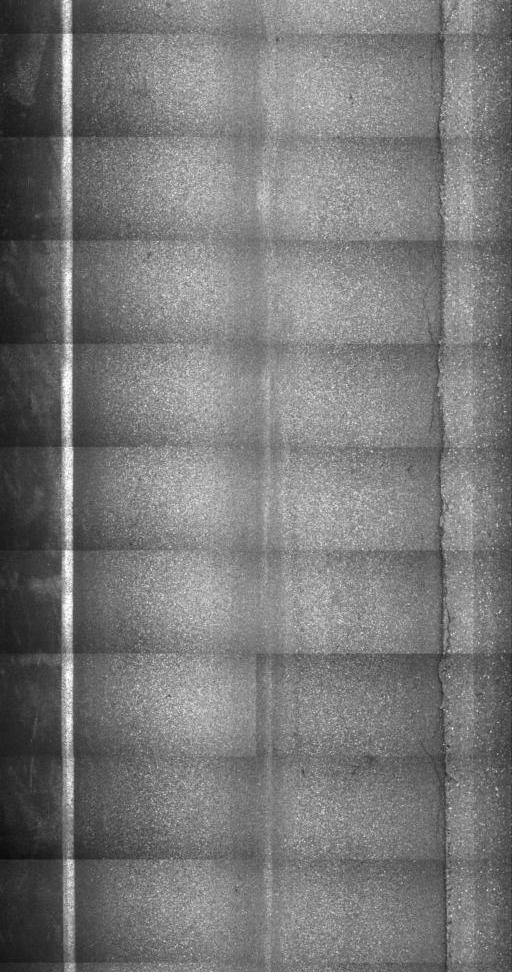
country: US
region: Vermont
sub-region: Washington County
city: Waterbury
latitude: 44.1973
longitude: -72.8930
